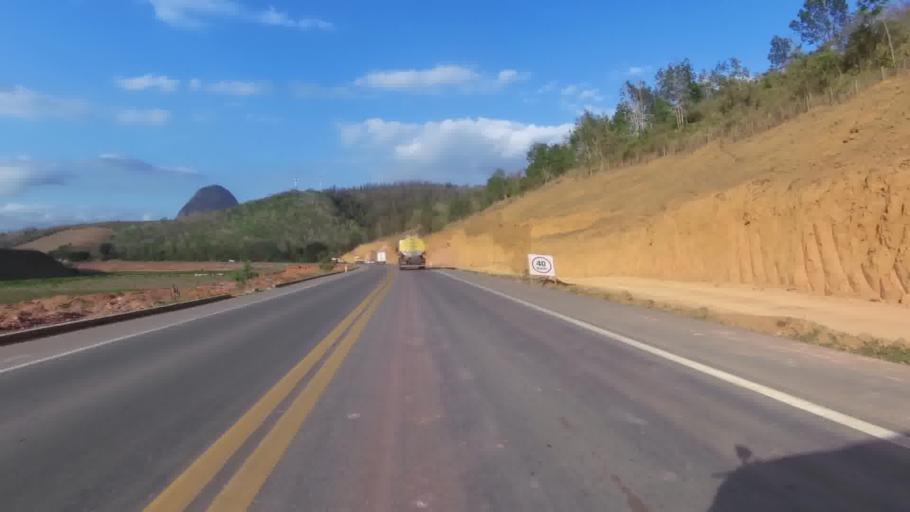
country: BR
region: Espirito Santo
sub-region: Cachoeiro De Itapemirim
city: Cachoeiro de Itapemirim
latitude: -20.8962
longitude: -41.0444
